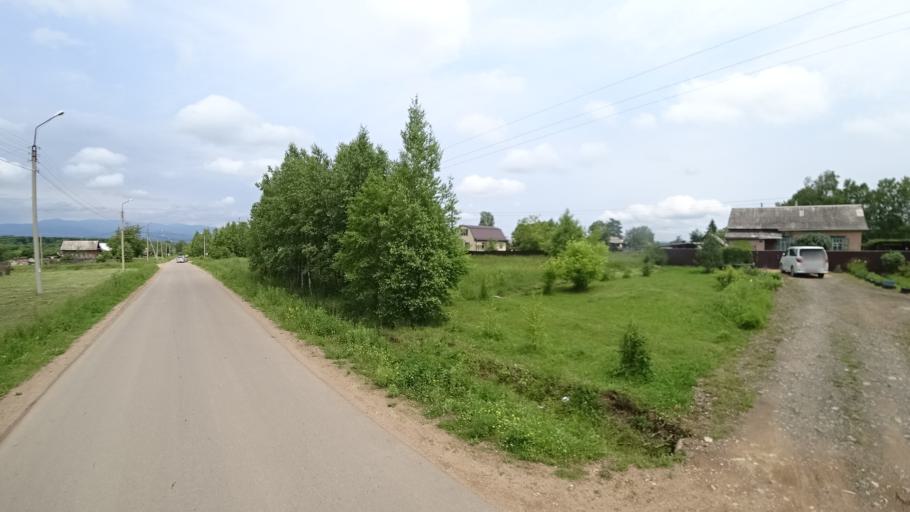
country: RU
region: Primorskiy
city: Novosysoyevka
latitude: 44.2345
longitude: 133.3593
